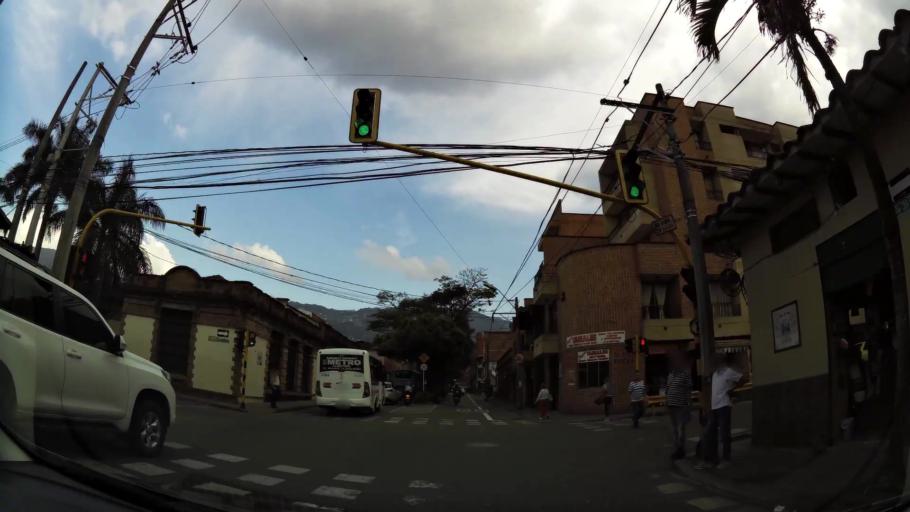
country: CO
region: Antioquia
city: Envigado
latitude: 6.1673
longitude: -75.5868
